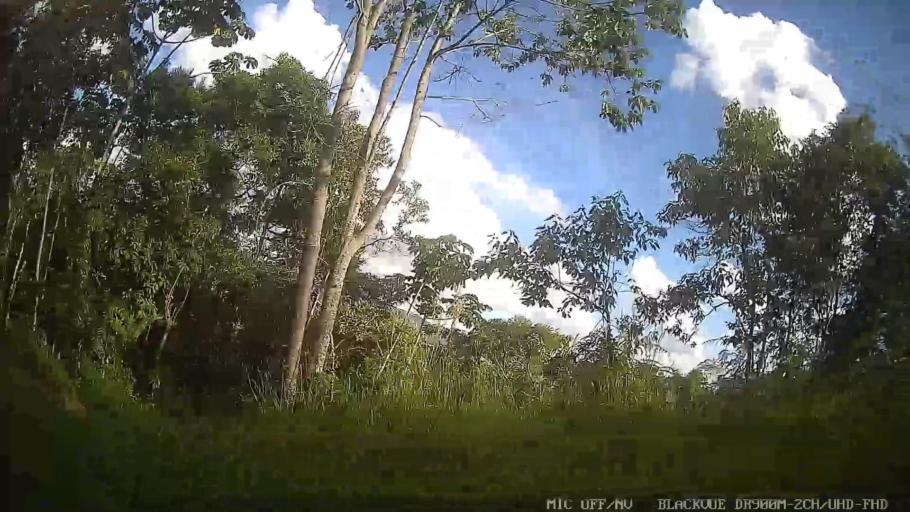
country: BR
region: Minas Gerais
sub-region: Extrema
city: Extrema
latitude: -22.8242
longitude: -46.2517
